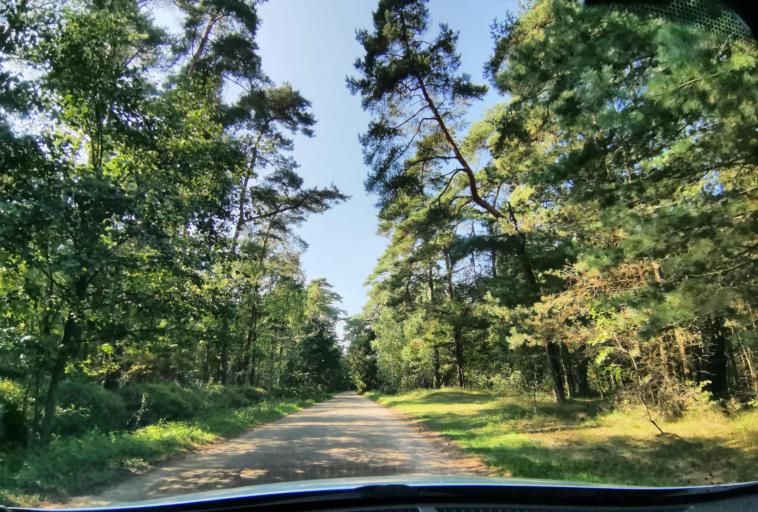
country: LT
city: Nida
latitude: 55.1619
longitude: 20.8261
